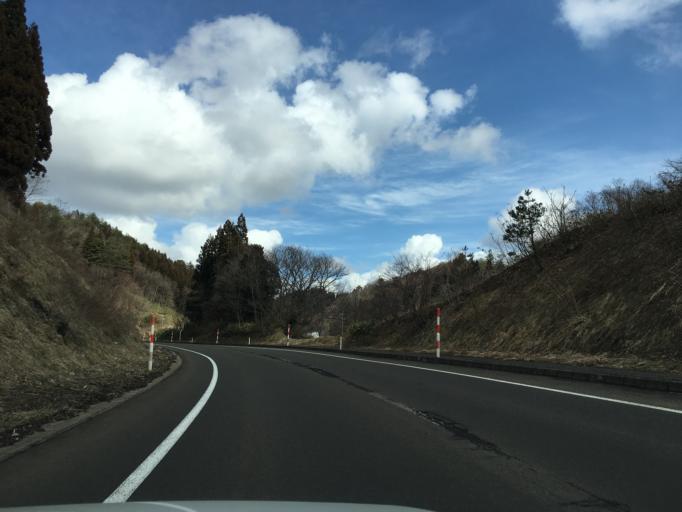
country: JP
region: Akita
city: Odate
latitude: 40.1864
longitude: 140.5123
